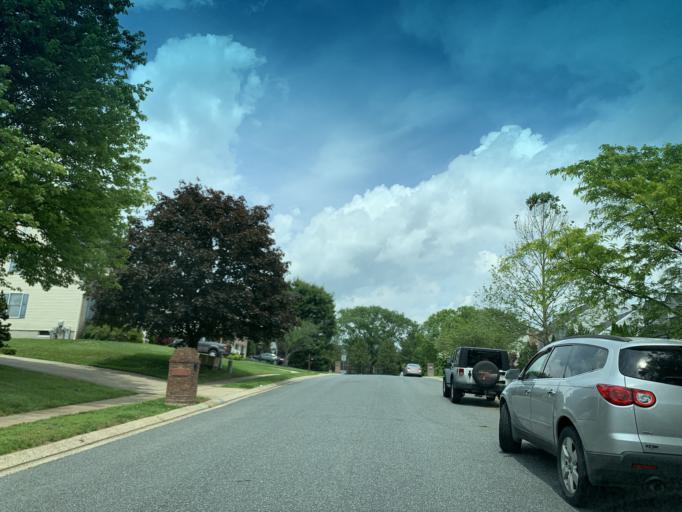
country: US
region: Maryland
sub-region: Harford County
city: South Bel Air
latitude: 39.5558
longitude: -76.3344
